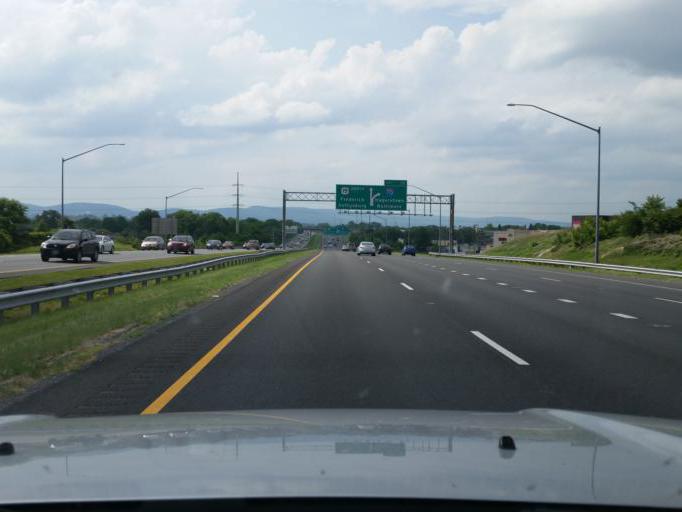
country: US
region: Maryland
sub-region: Frederick County
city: Ballenger Creek
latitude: 39.3859
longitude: -77.4132
